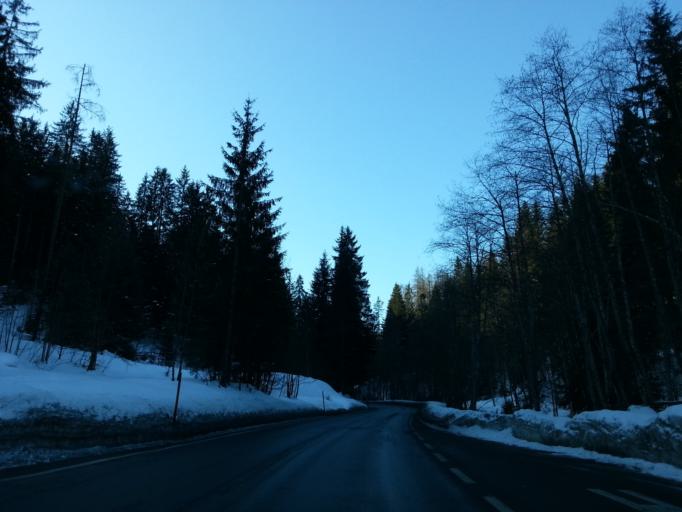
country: AT
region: Salzburg
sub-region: Politischer Bezirk Sankt Johann im Pongau
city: Eben im Pongau
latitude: 47.4879
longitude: 13.3966
